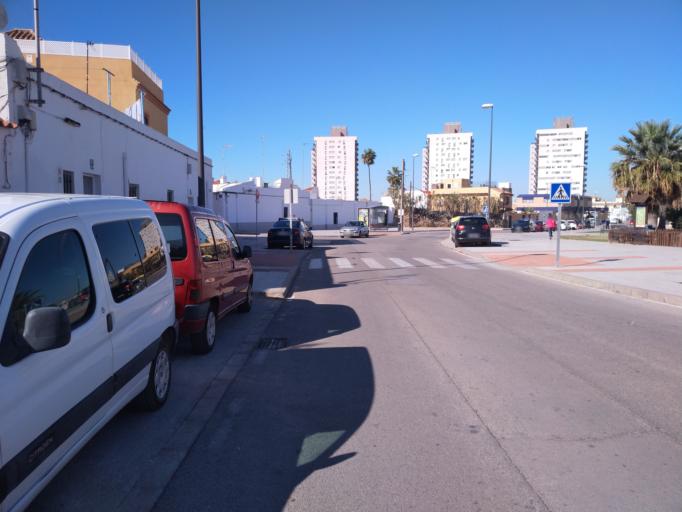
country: ES
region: Andalusia
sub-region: Provincia de Cadiz
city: San Fernando
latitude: 36.4810
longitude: -6.1975
